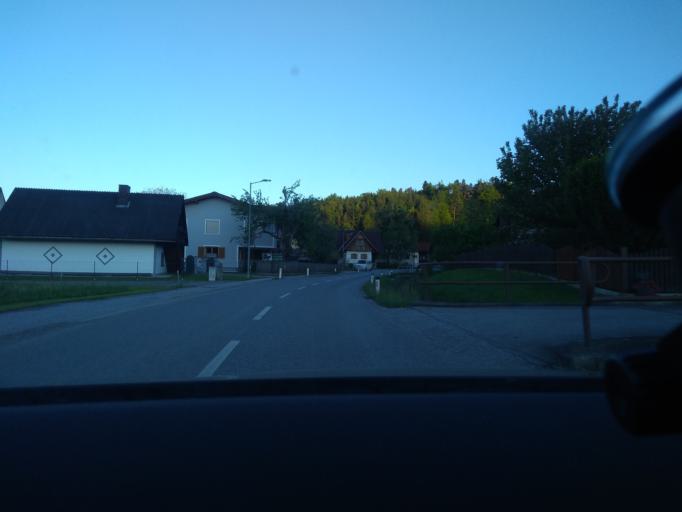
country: AT
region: Styria
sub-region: Politischer Bezirk Voitsberg
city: Mooskirchen
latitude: 46.9753
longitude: 15.2838
